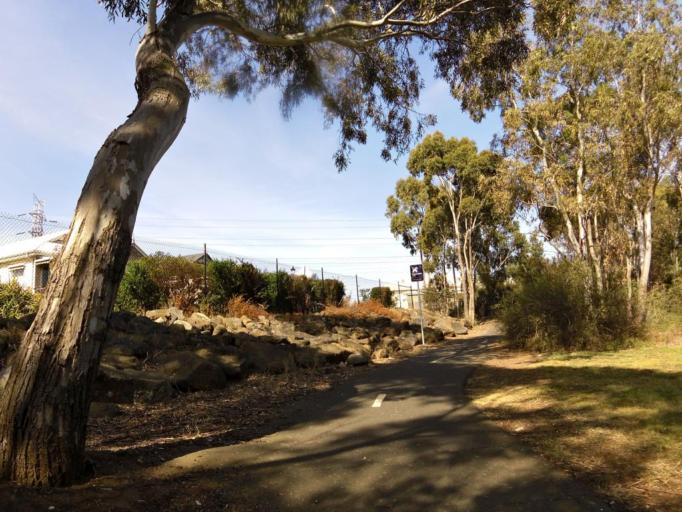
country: AU
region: Victoria
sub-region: Brimbank
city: Sunshine West
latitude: -37.7784
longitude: 144.8094
